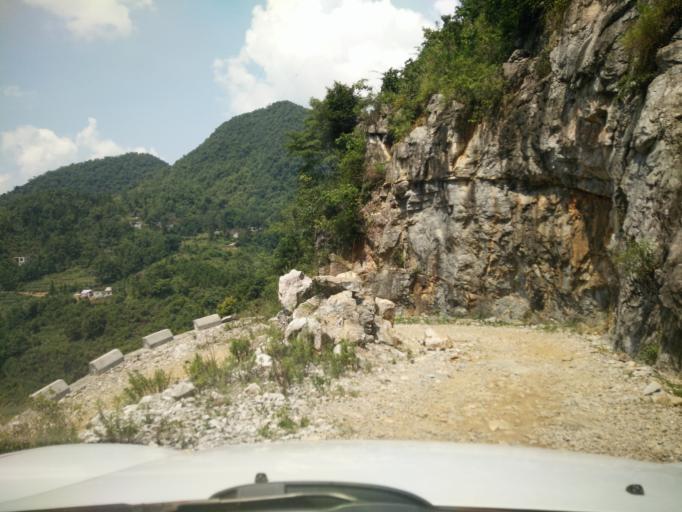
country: CN
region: Guangxi Zhuangzu Zizhiqu
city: Xinzhou
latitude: 25.0225
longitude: 105.7047
